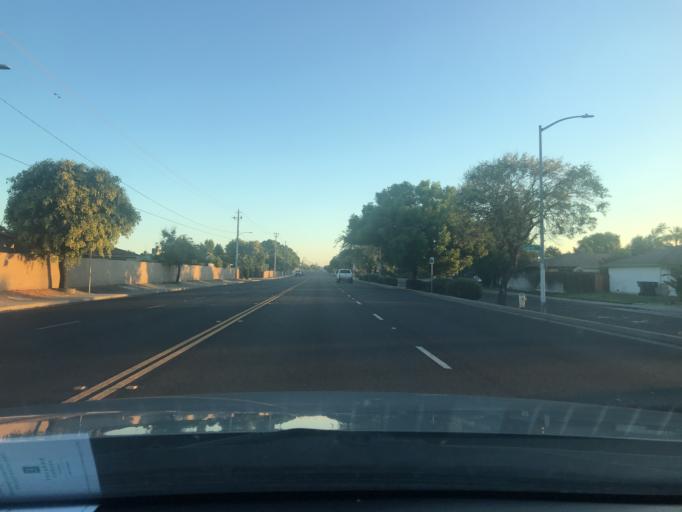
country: US
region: California
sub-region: Merced County
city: Atwater
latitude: 37.3517
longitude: -120.5959
